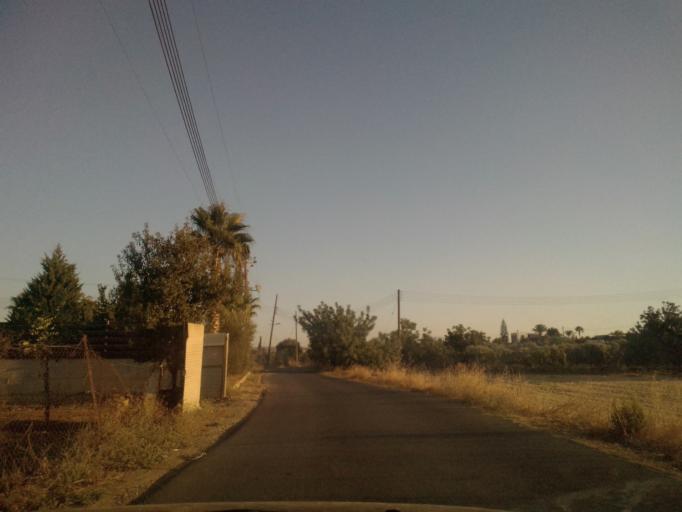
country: CY
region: Limassol
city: Ypsonas
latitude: 34.6780
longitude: 32.9619
